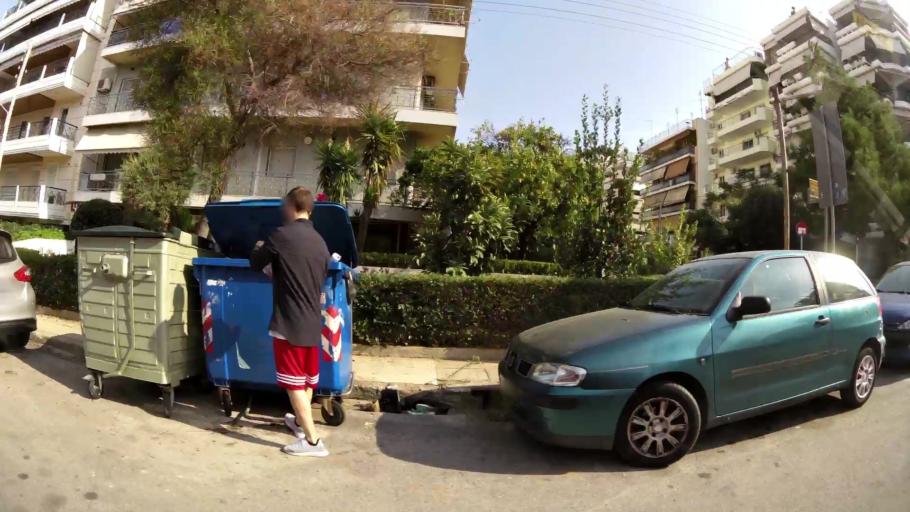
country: GR
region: Attica
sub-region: Nomarchia Athinas
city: Nea Smyrni
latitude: 37.9437
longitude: 23.7069
